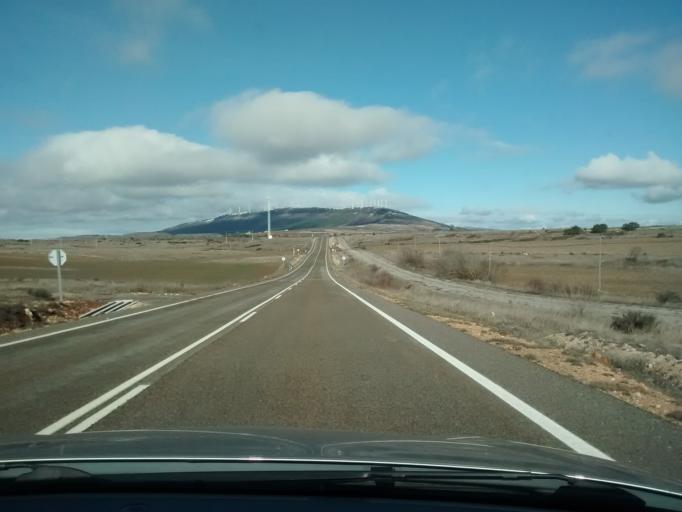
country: ES
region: Castille and Leon
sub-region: Provincia de Burgos
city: Rucandio
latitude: 42.7838
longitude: -3.6194
